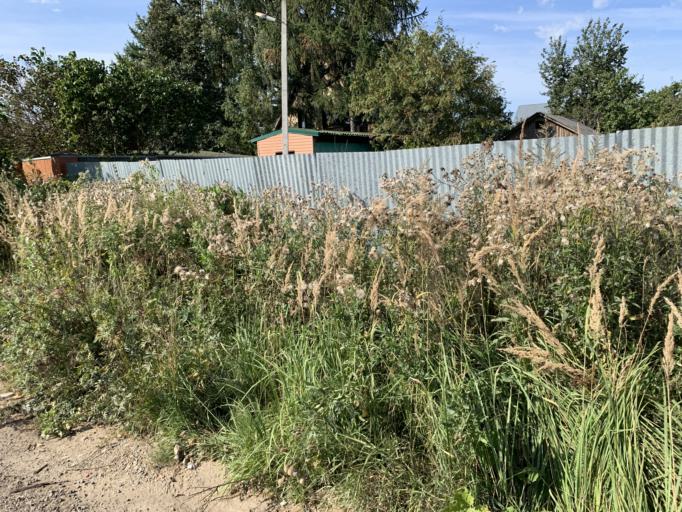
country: RU
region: Moskovskaya
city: Lesnyye Polyany
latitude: 55.9836
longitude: 37.8516
